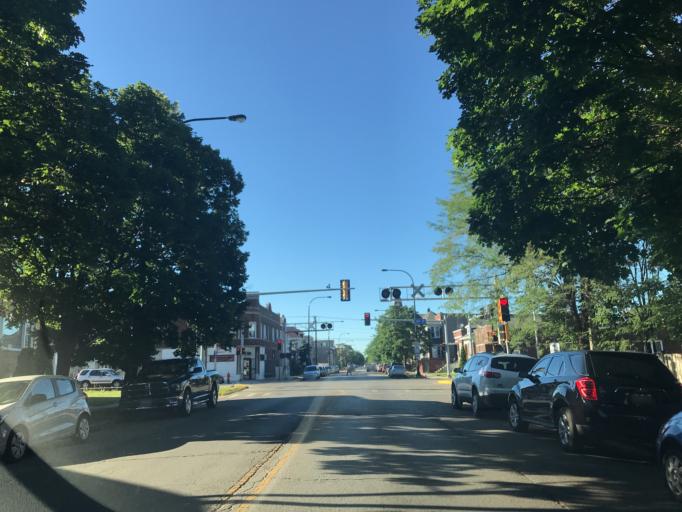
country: US
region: Illinois
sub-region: Cook County
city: Cicero
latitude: 41.8579
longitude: -87.7494
